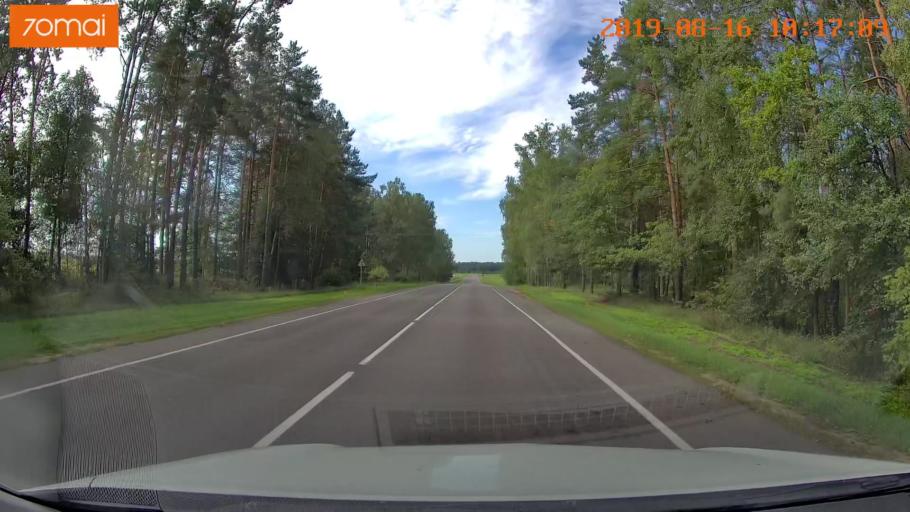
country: BY
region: Mogilev
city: Asipovichy
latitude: 53.3145
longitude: 28.7150
